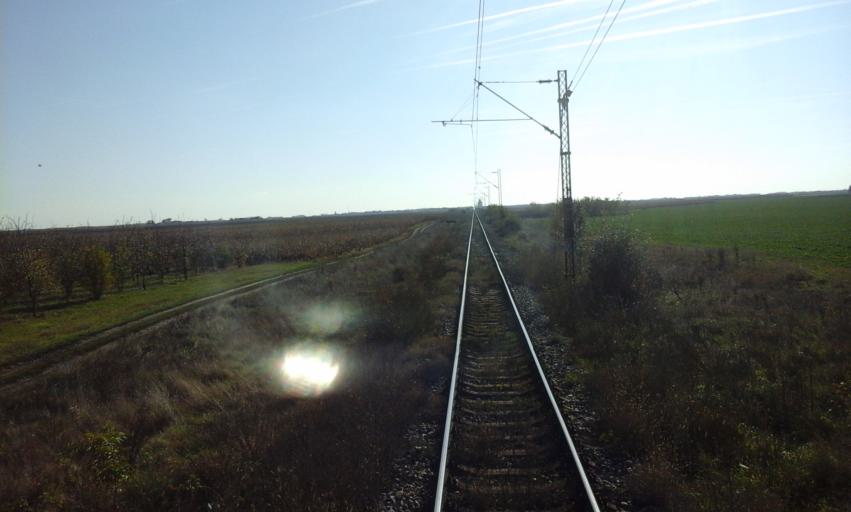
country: RS
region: Autonomna Pokrajina Vojvodina
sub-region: Severnobacki Okrug
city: Subotica
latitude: 45.9805
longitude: 19.6745
